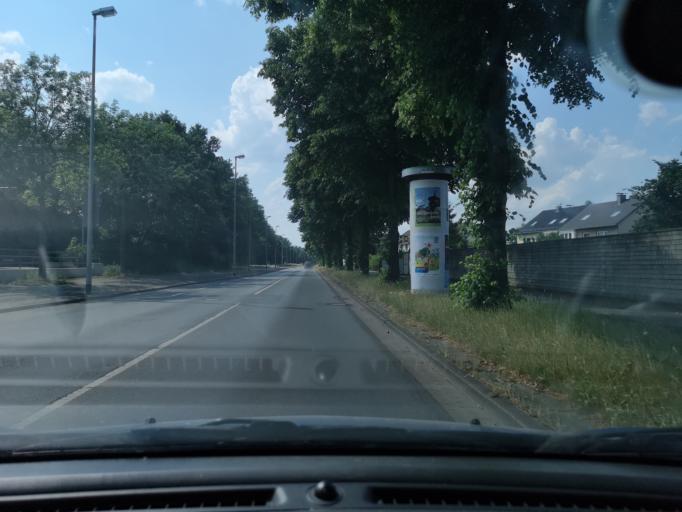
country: DE
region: Lower Saxony
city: Langenhagen
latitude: 52.4187
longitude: 9.7649
